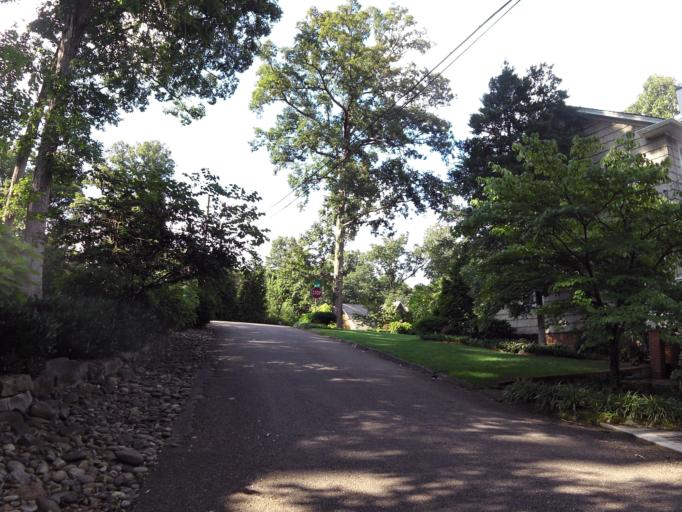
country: US
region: Tennessee
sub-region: Knox County
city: Knoxville
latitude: 35.9424
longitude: -83.9682
